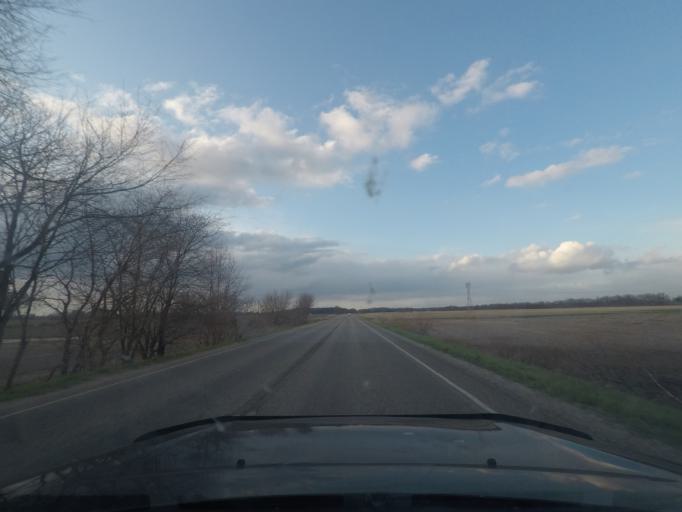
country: US
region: Indiana
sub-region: LaPorte County
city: Kingsford Heights
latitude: 41.5309
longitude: -86.7407
